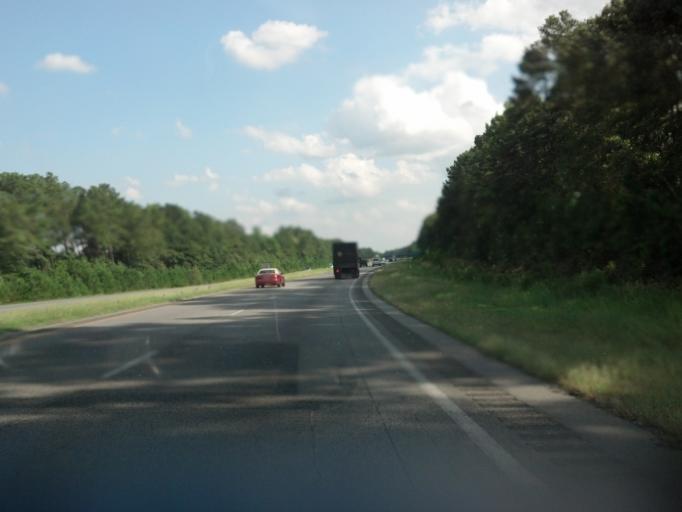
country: US
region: North Carolina
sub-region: Nash County
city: Rocky Mount
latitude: 35.9562
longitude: -77.7658
